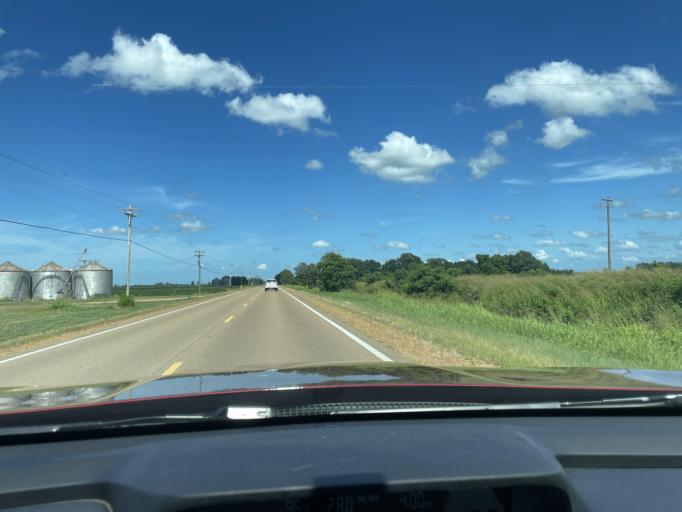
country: US
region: Mississippi
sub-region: Humphreys County
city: Belzoni
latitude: 33.1837
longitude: -90.5658
